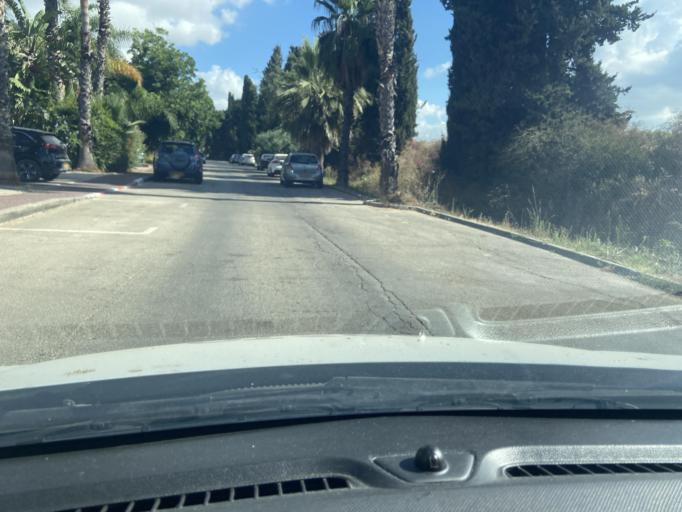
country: IL
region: Central District
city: Yehud
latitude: 32.0371
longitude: 34.8988
